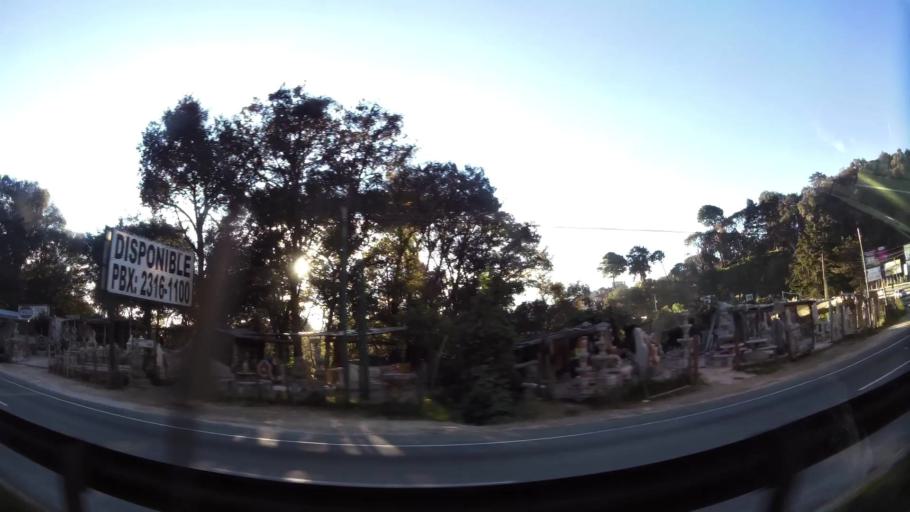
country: GT
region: Sacatepequez
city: San Lucas Sacatepequez
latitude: 14.6121
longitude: -90.6501
